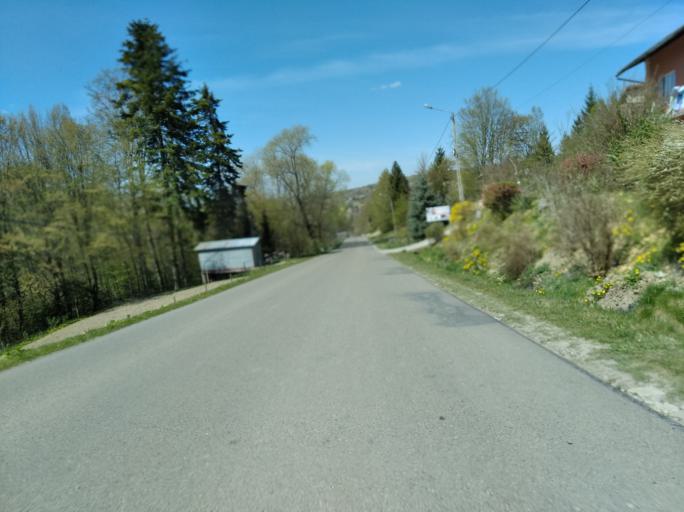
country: PL
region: Subcarpathian Voivodeship
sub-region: Powiat brzozowski
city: Golcowa
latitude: 49.7619
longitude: 22.0559
